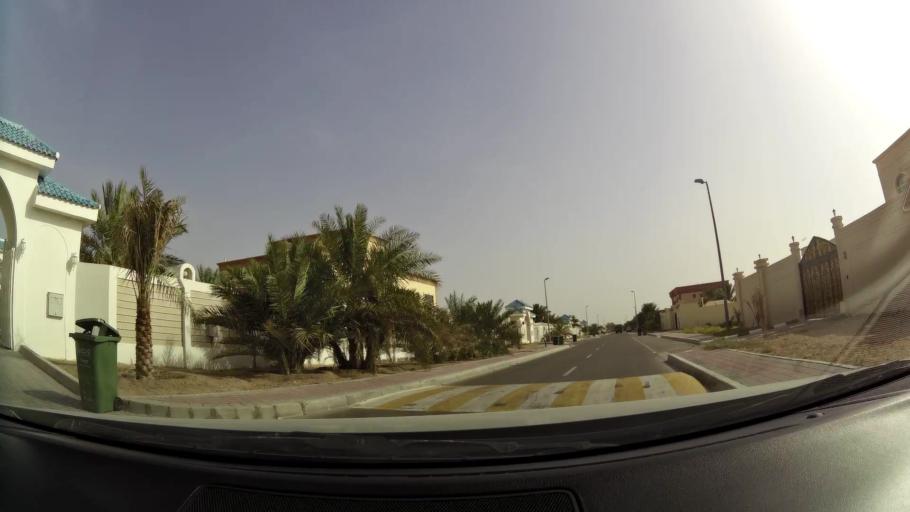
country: AE
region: Abu Dhabi
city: Al Ain
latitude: 24.1345
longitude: 55.7039
